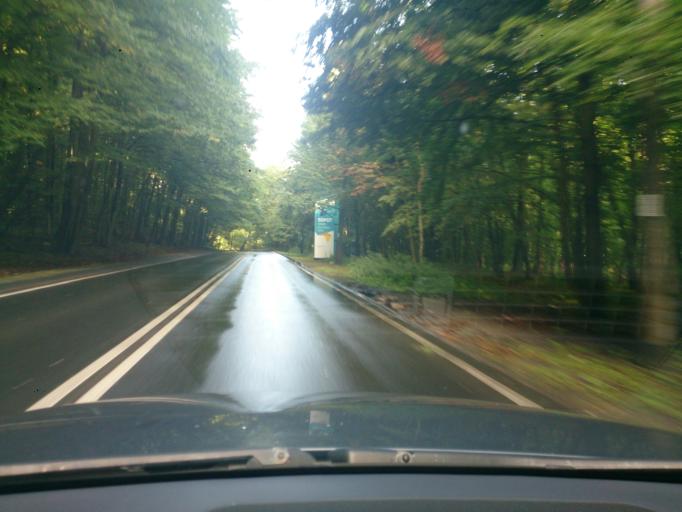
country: PL
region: Pomeranian Voivodeship
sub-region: Sopot
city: Sopot
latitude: 54.4562
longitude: 18.5256
